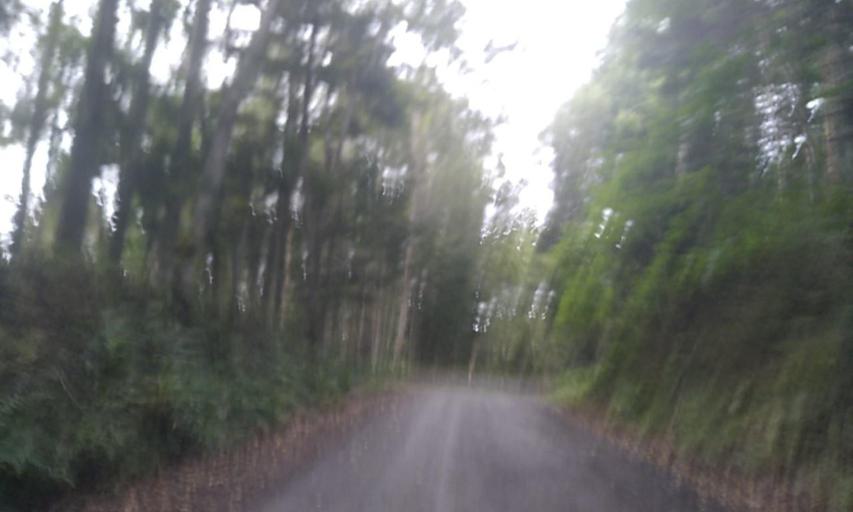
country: JP
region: Hokkaido
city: Abashiri
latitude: 43.6582
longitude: 144.5505
